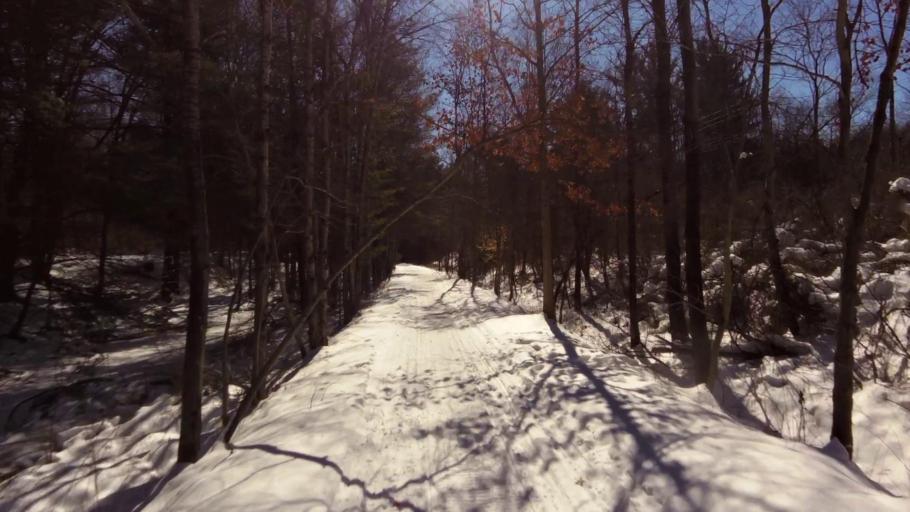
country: US
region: New York
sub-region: Allegany County
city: Houghton
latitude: 42.3594
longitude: -78.1329
